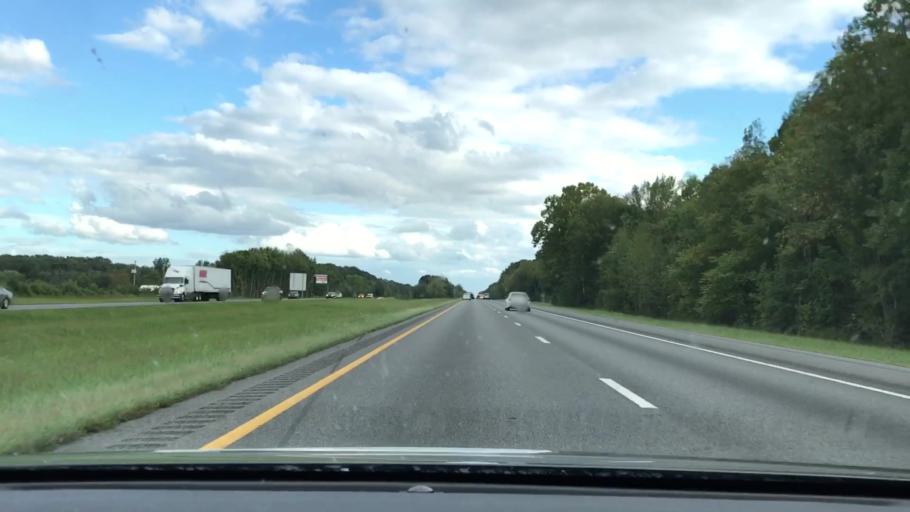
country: US
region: Kentucky
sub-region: Todd County
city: Guthrie
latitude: 36.5067
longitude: -87.1950
